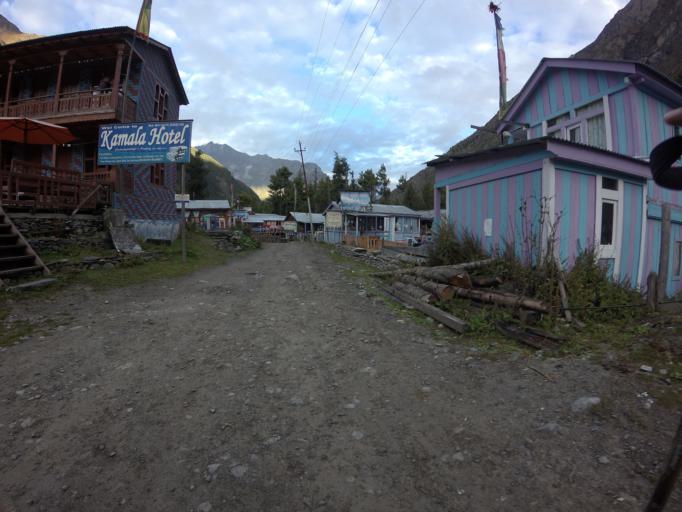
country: NP
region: Western Region
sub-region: Gandaki Zone
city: Pisang
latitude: 28.6022
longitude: 84.1798
